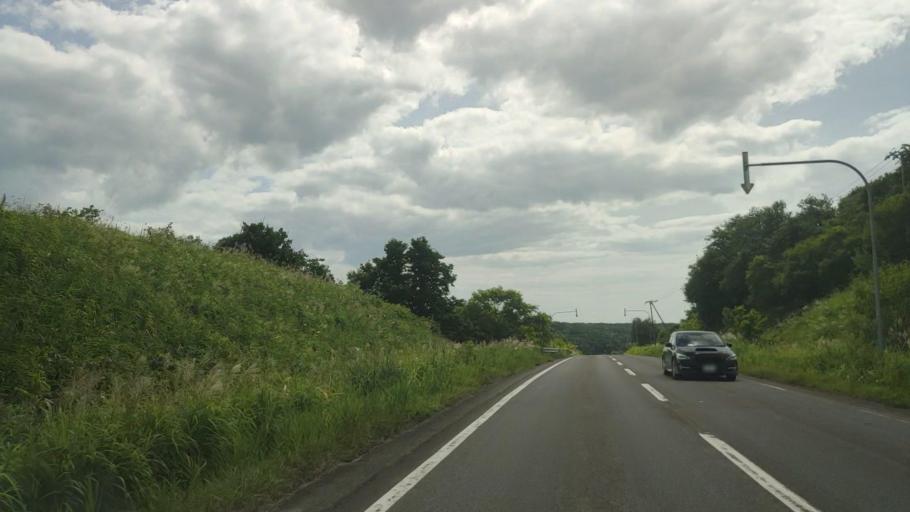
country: JP
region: Hokkaido
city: Rumoi
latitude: 44.6124
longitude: 141.8000
